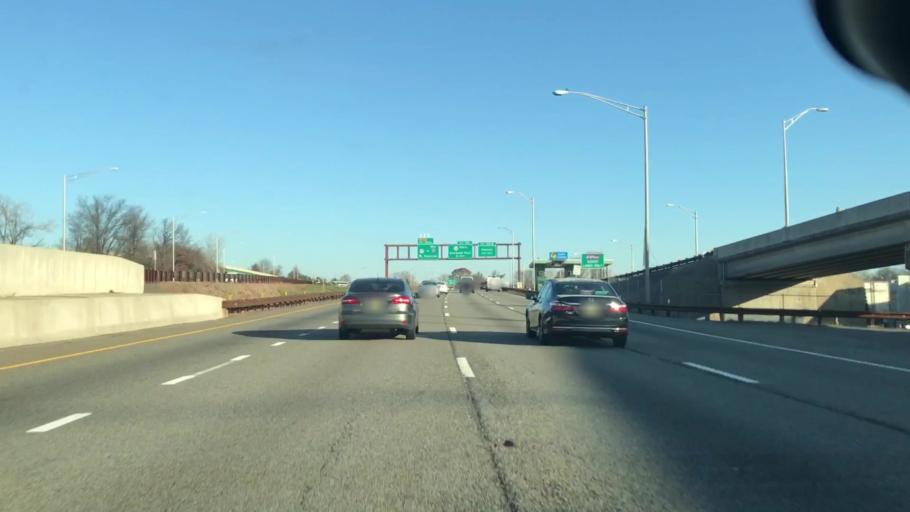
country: US
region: New Jersey
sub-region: Passaic County
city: Clifton
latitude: 40.8771
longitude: -74.1662
